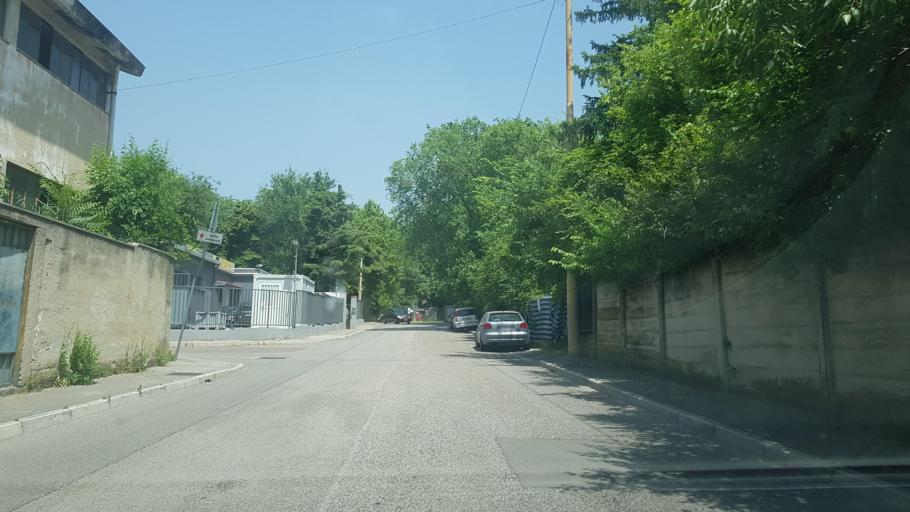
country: IT
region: Friuli Venezia Giulia
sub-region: Provincia di Trieste
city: Domio
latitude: 45.6175
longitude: 13.8208
